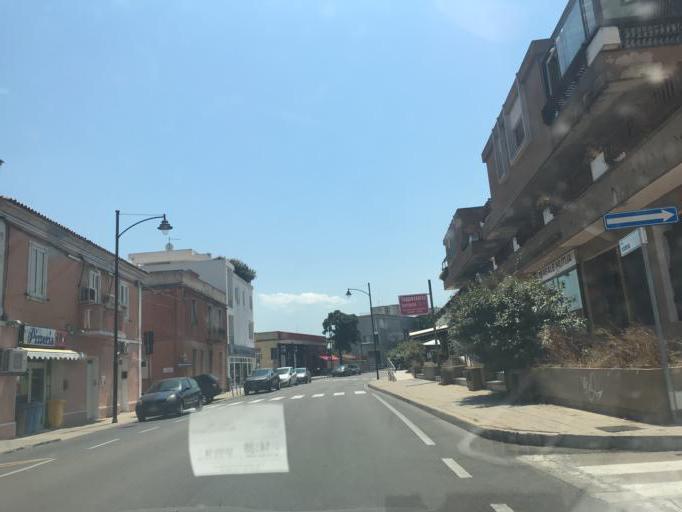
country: IT
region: Sardinia
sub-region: Provincia di Olbia-Tempio
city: Olbia
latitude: 40.9198
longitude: 9.4972
